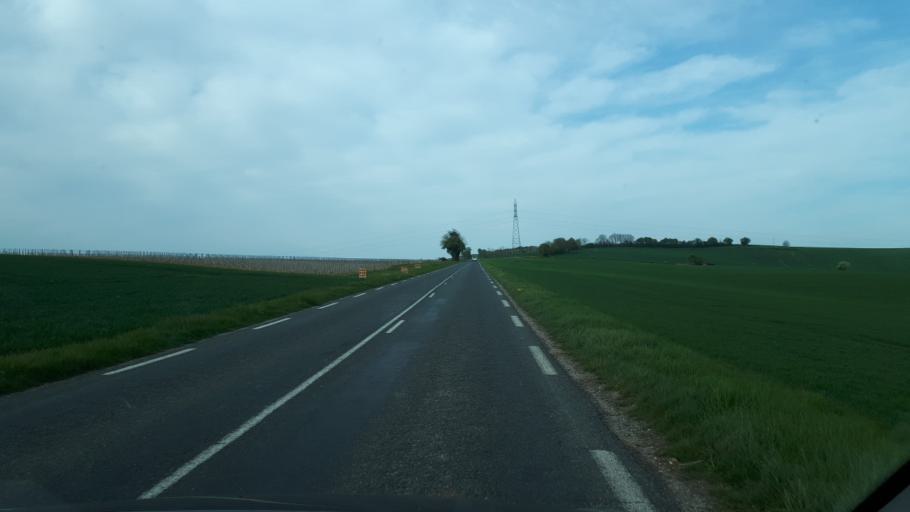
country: FR
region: Centre
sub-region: Departement du Cher
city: Sancerre
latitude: 47.2662
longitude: 2.7202
